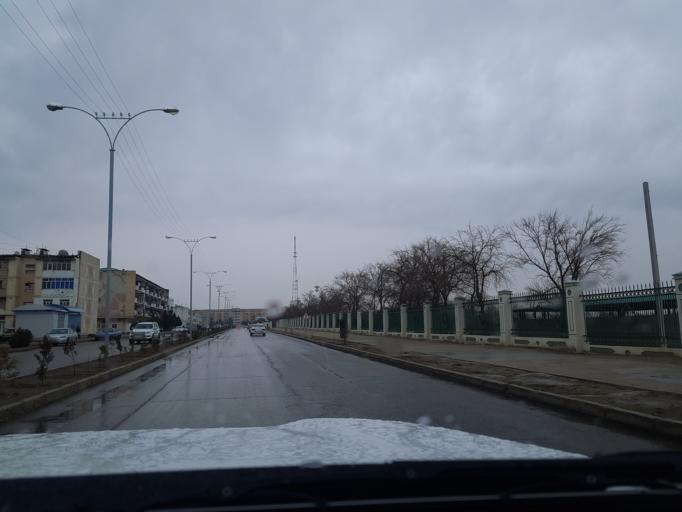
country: TM
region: Balkan
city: Balkanabat
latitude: 39.5211
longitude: 54.3582
